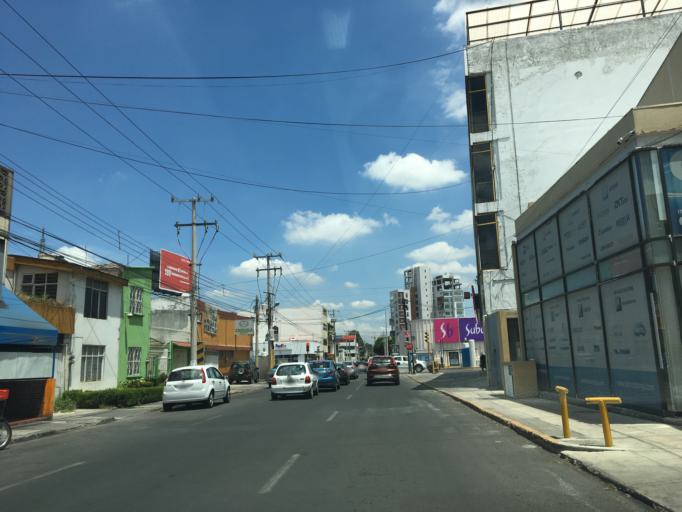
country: MX
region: Puebla
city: Puebla
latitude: 19.0556
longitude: -98.2205
